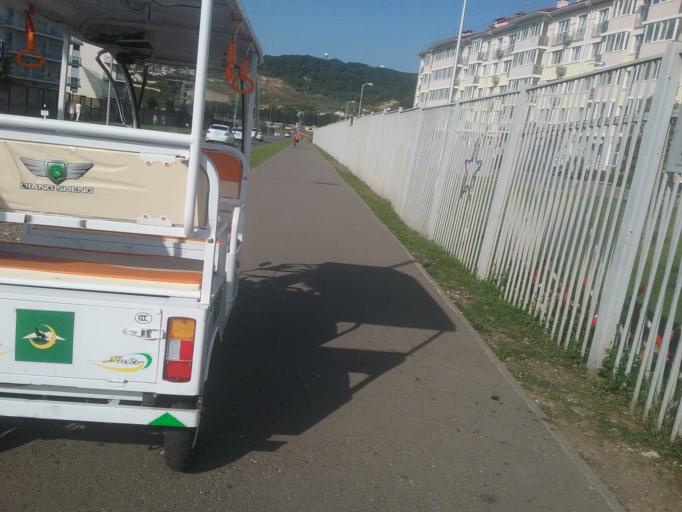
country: RU
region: Krasnodarskiy
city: Adler
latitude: 43.4016
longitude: 39.9781
